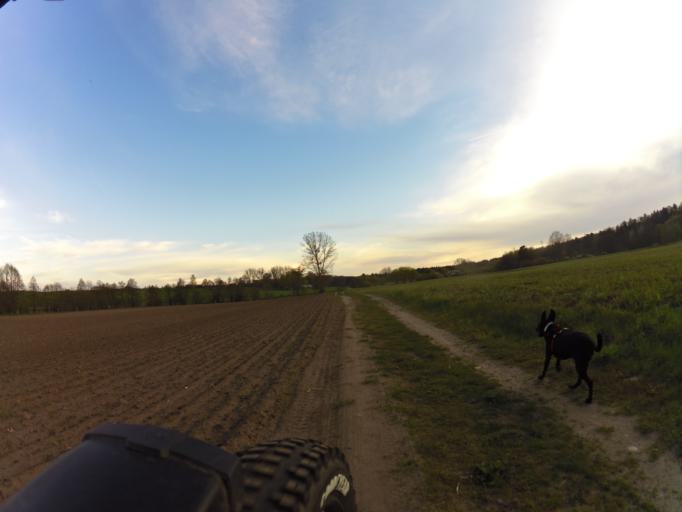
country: PL
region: West Pomeranian Voivodeship
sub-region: Powiat lobeski
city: Lobez
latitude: 53.7066
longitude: 15.6484
